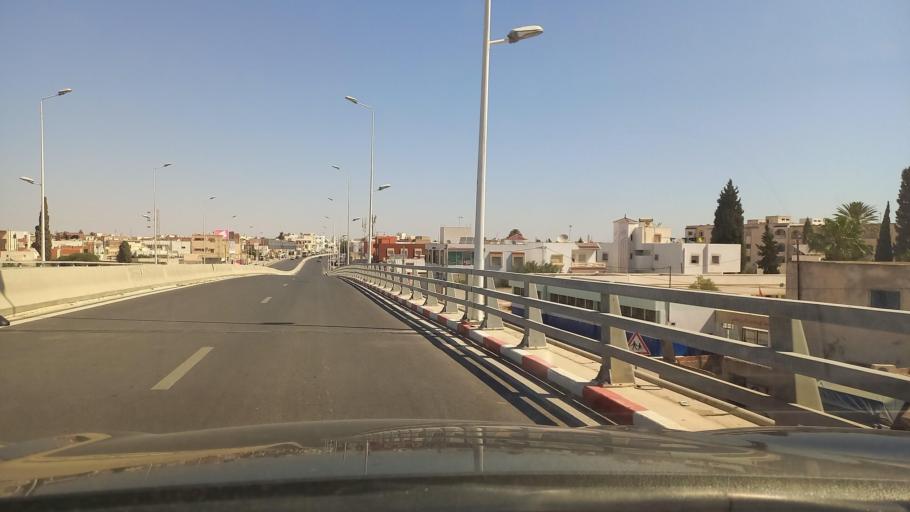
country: TN
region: Safaqis
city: Sfax
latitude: 34.7337
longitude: 10.7245
